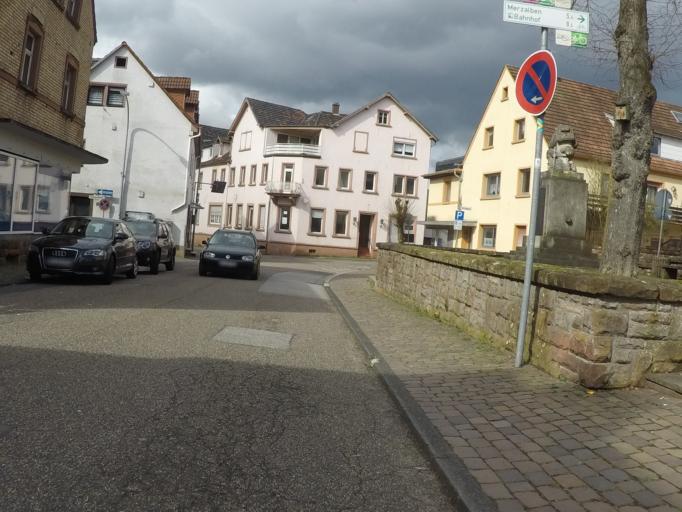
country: DE
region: Rheinland-Pfalz
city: Munchweiler an der Rodalbe
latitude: 49.2186
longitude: 7.7029
